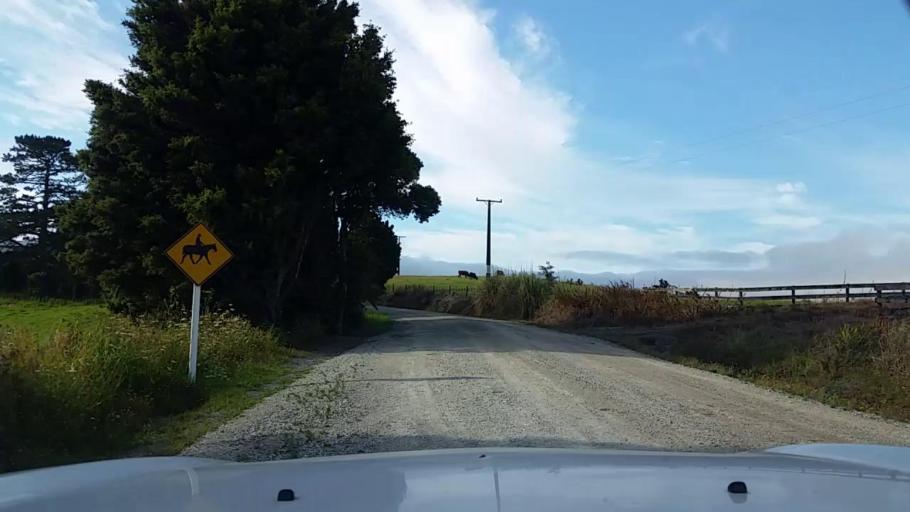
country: NZ
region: Northland
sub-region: Whangarei
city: Maungatapere
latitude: -35.6678
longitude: 174.1745
